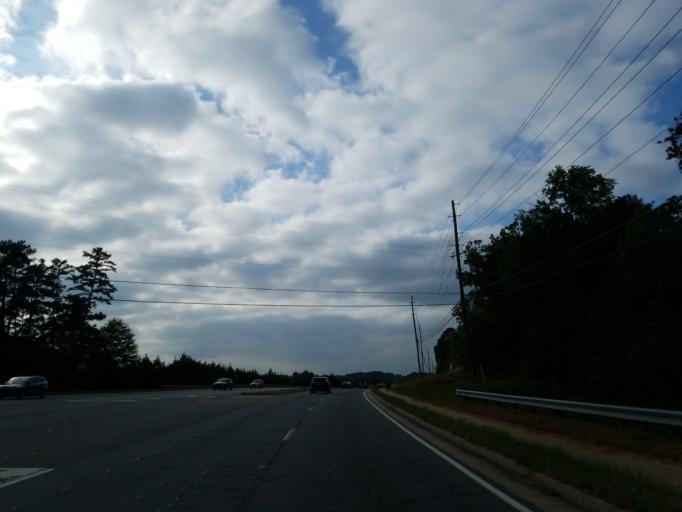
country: US
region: Georgia
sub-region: Cobb County
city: Kennesaw
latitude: 34.0895
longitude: -84.6070
